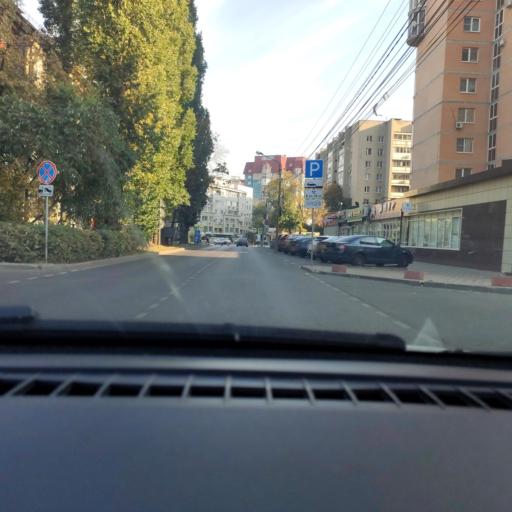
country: RU
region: Voronezj
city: Voronezh
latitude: 51.6672
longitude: 39.1859
